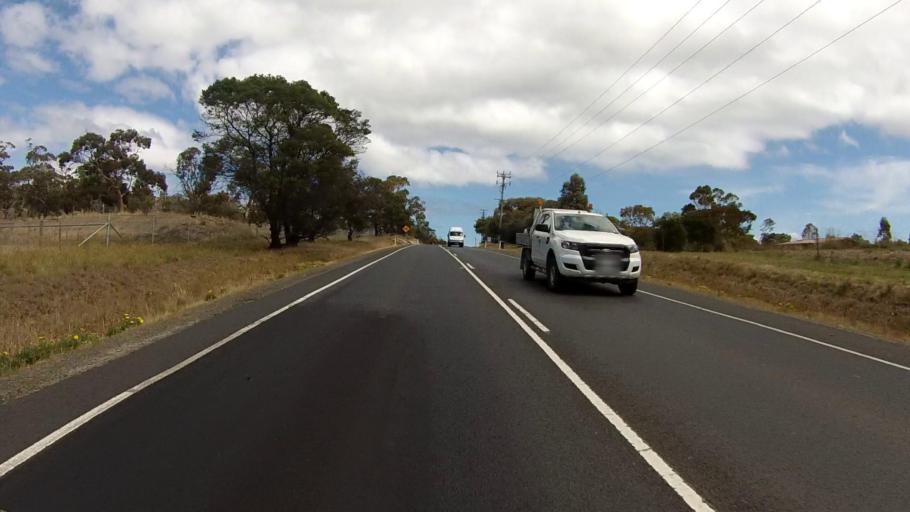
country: AU
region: Tasmania
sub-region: Sorell
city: Sorell
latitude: -42.8157
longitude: 147.6251
